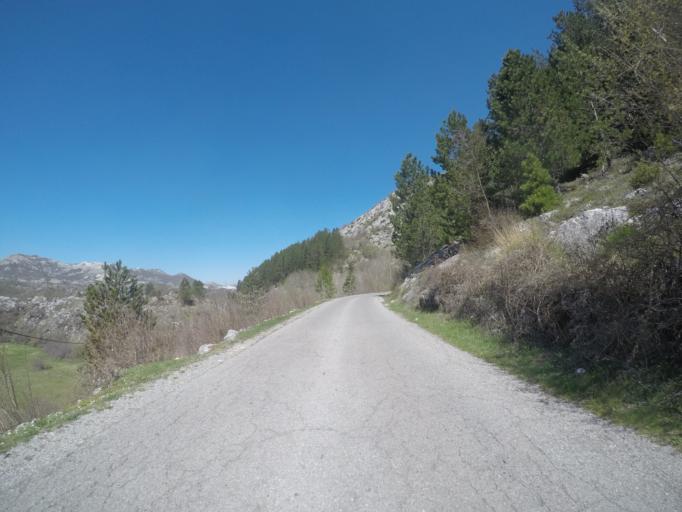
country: ME
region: Cetinje
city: Cetinje
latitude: 42.4592
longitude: 18.8683
